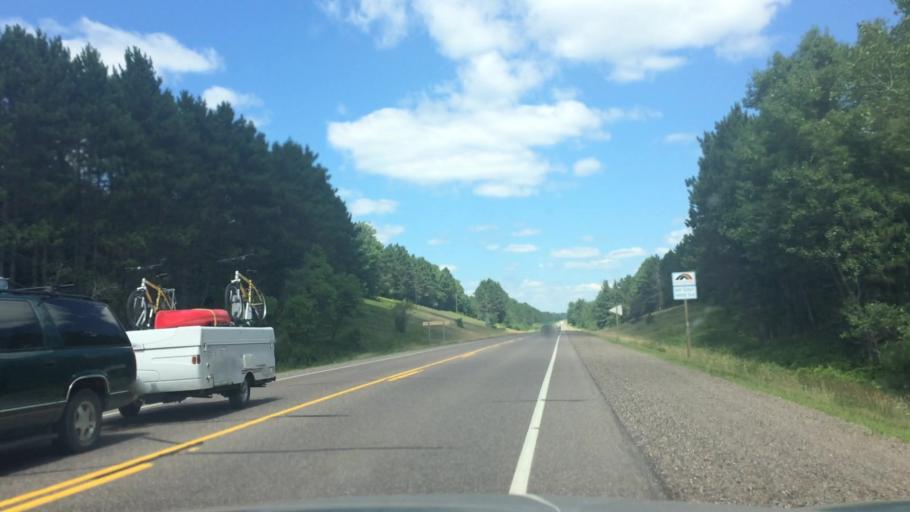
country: US
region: Wisconsin
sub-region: Vilas County
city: Lac du Flambeau
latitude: 45.9531
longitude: -89.7007
